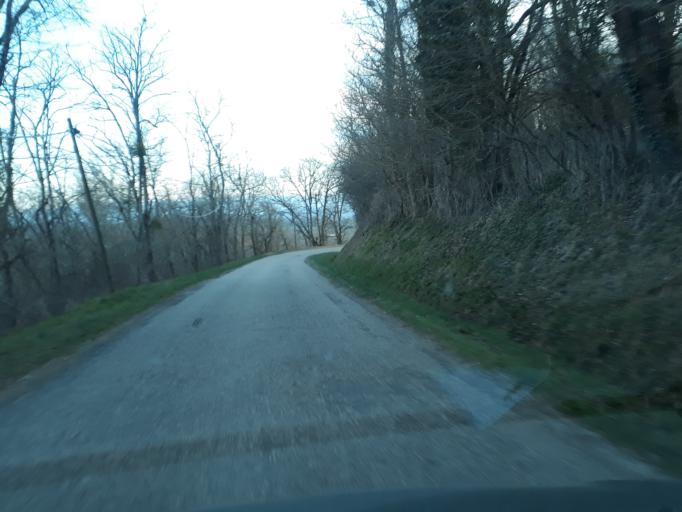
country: FR
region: Midi-Pyrenees
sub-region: Departement de la Haute-Garonne
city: Montesquieu-Volvestre
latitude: 43.1737
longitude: 1.3222
